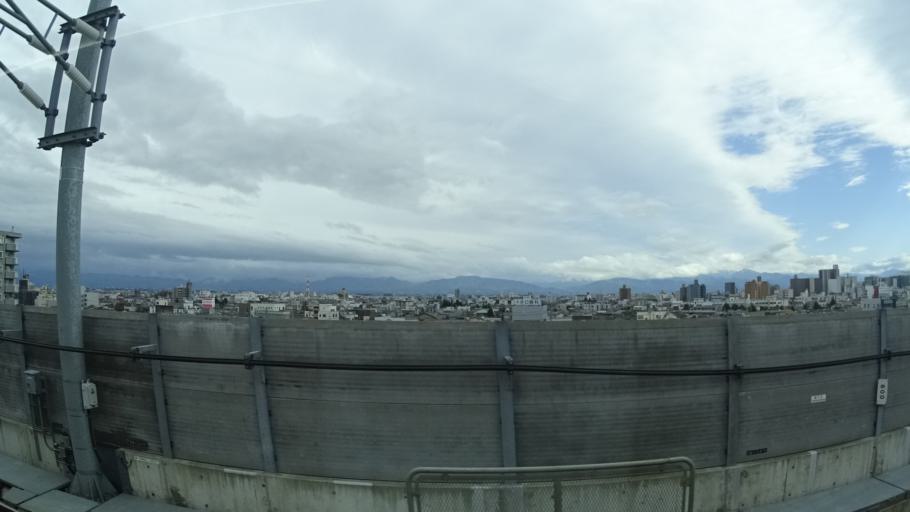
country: JP
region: Toyama
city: Toyama-shi
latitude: 36.6984
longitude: 137.2242
